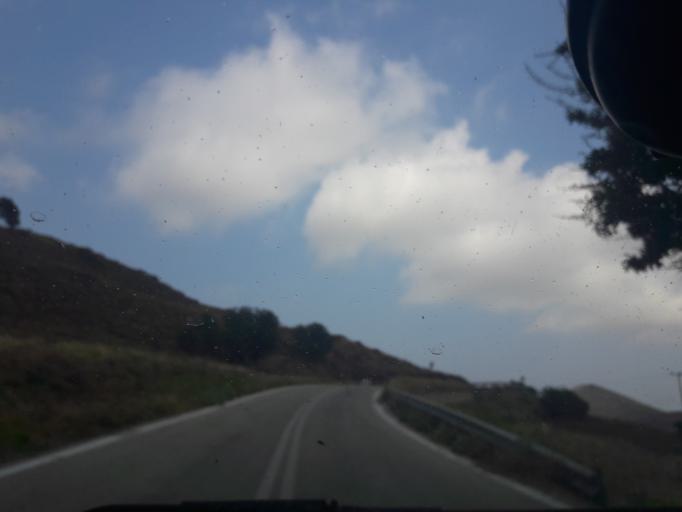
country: GR
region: North Aegean
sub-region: Nomos Lesvou
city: Myrina
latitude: 39.9542
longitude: 25.1677
